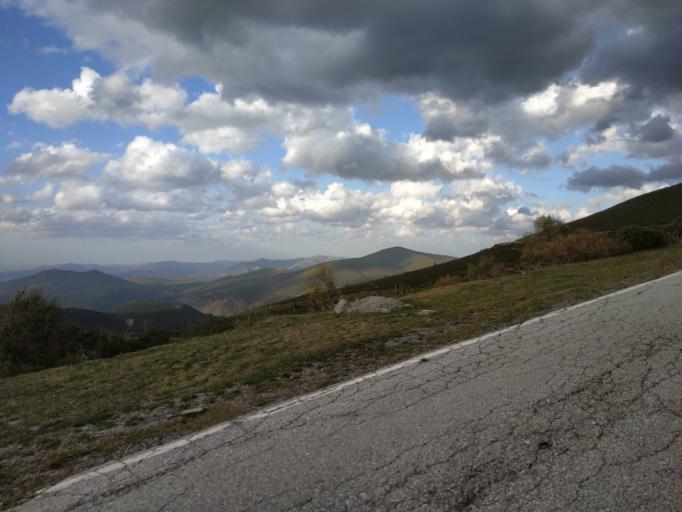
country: ES
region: Castille and Leon
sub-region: Provincia de Leon
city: Candin
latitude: 42.8678
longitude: -6.8232
